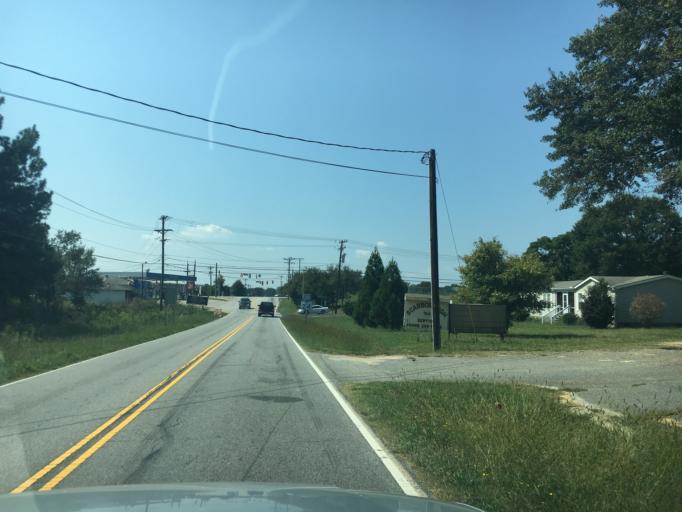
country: US
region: South Carolina
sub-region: Anderson County
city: Centerville
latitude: 34.5112
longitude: -82.7540
